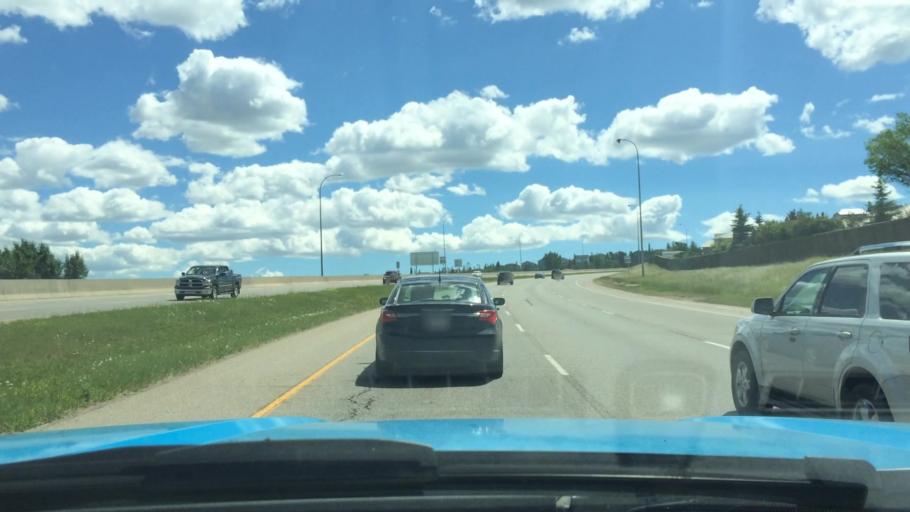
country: CA
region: Alberta
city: Calgary
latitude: 51.1399
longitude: -114.1216
